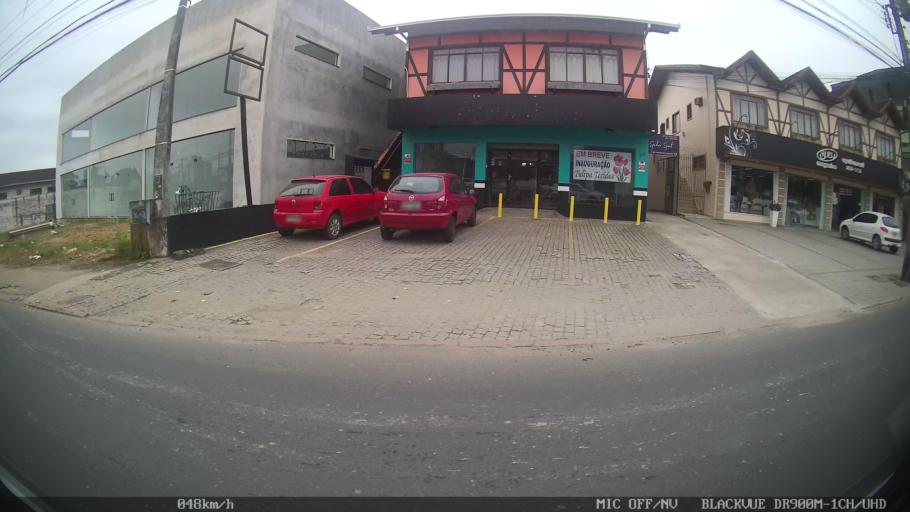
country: BR
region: Santa Catarina
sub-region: Joinville
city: Joinville
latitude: -26.3238
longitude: -48.8447
